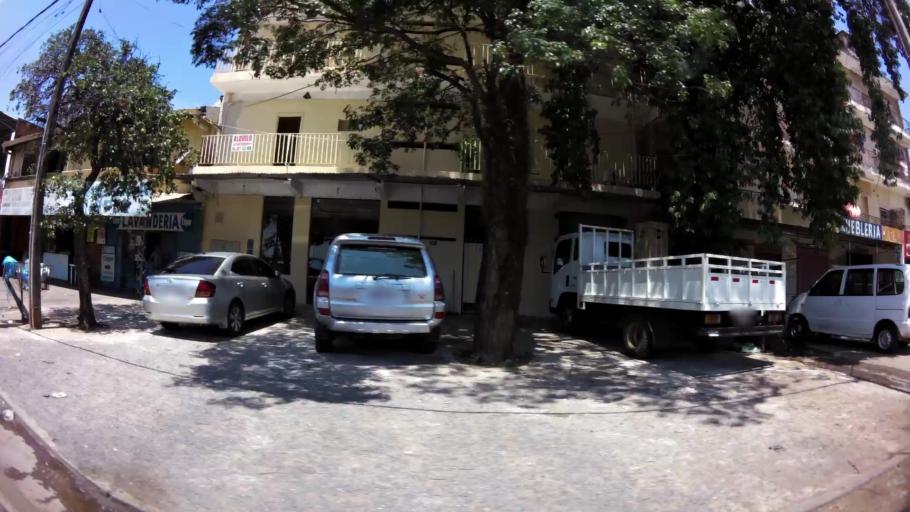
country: PY
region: Central
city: Lambare
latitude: -25.3387
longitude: -57.5840
